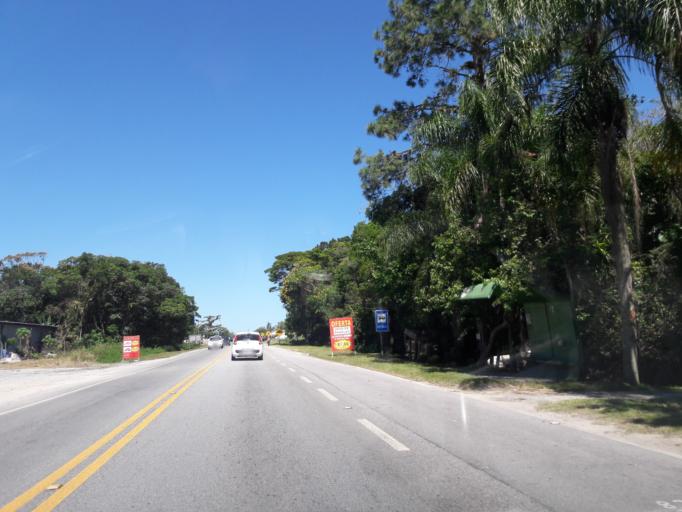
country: BR
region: Parana
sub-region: Pontal Do Parana
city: Pontal do Parana
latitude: -25.6899
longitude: -48.4868
